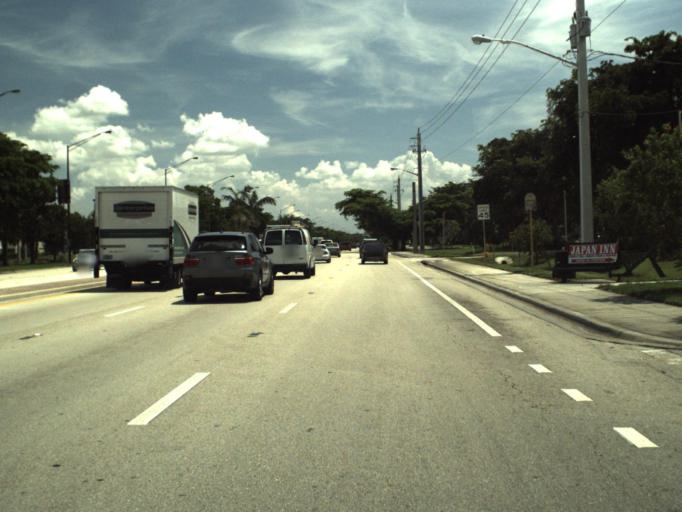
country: US
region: Florida
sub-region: Broward County
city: Plantation
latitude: 26.1478
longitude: -80.2572
